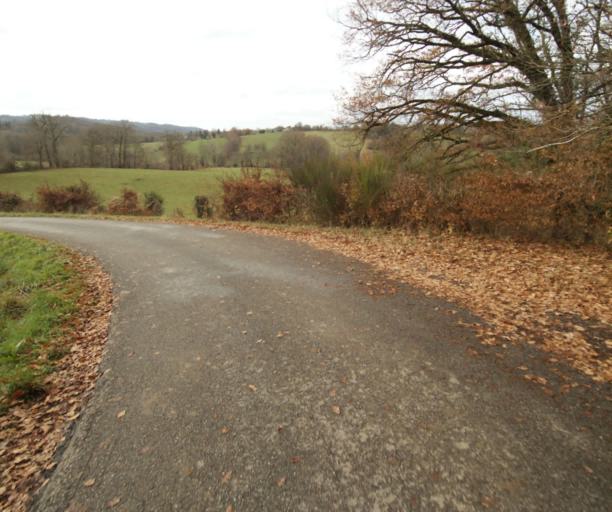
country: FR
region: Limousin
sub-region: Departement de la Correze
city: Saint-Mexant
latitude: 45.2653
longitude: 1.6138
